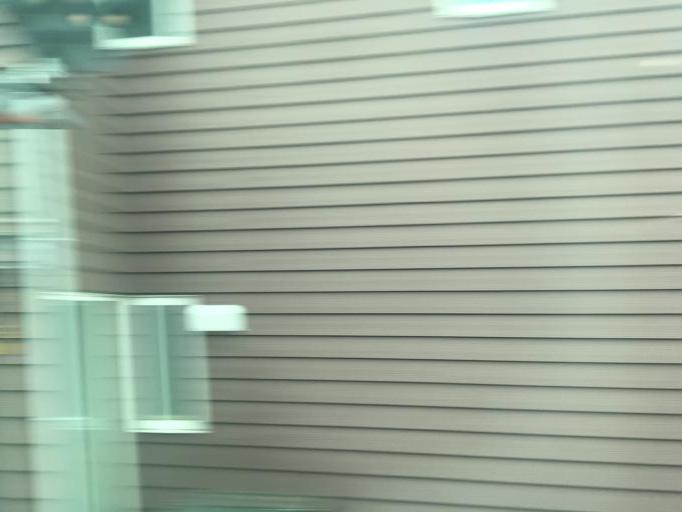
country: JP
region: Tokyo
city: Kokubunji
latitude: 35.6677
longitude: 139.4645
